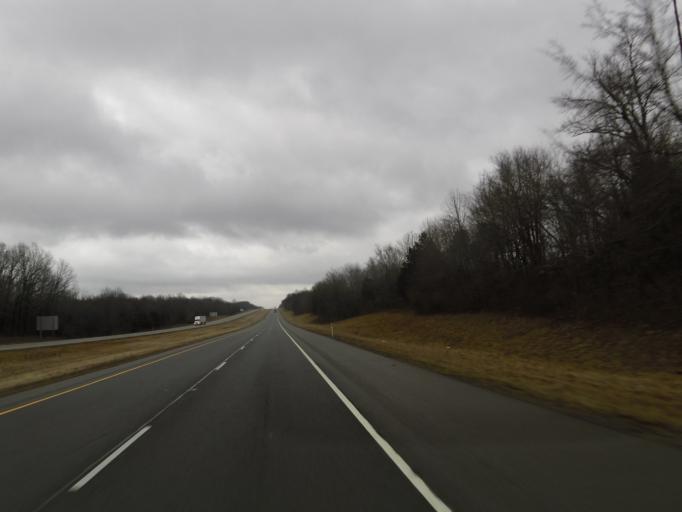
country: US
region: Illinois
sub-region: Johnson County
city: Vienna
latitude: 37.3949
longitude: -88.8444
